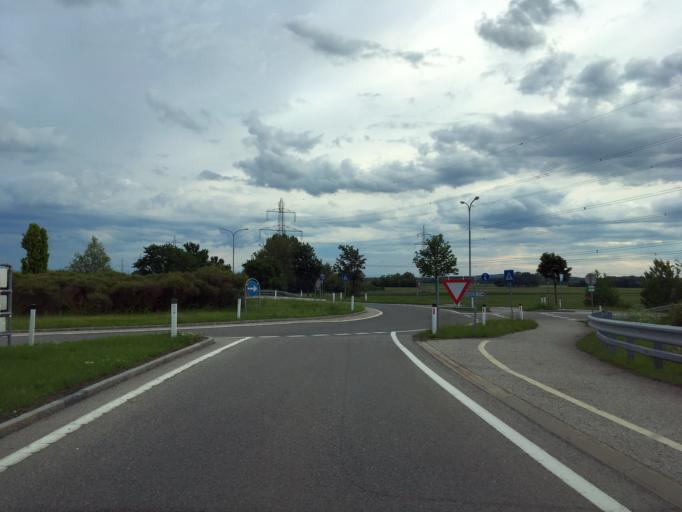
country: AT
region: Lower Austria
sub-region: Politischer Bezirk Tulln
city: Kirchberg am Wagram
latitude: 48.4054
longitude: 15.8804
